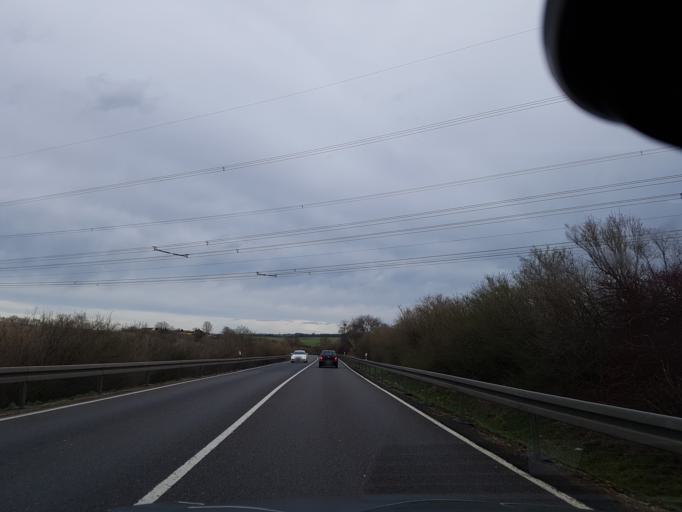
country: DE
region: Saxony
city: Dobeln
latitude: 51.1668
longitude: 13.1299
